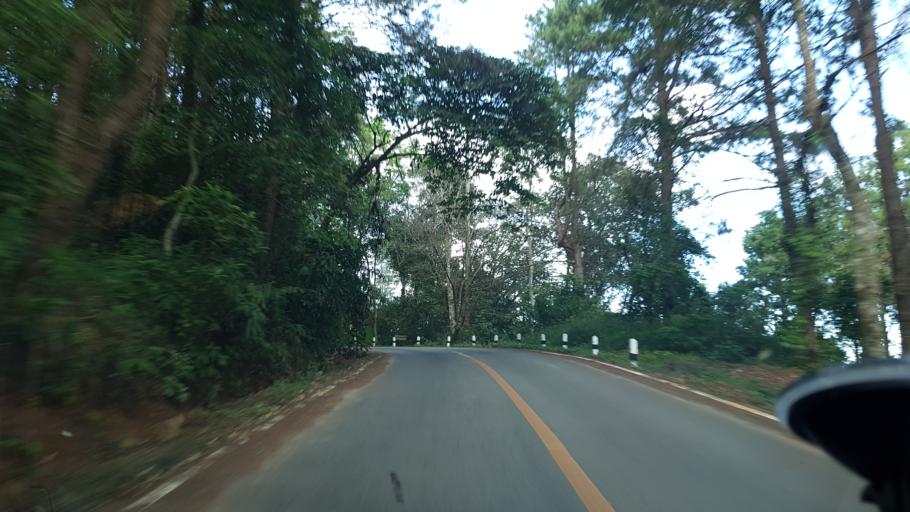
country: TH
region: Chiang Rai
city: Mae Fa Luang
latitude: 20.3307
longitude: 99.8152
